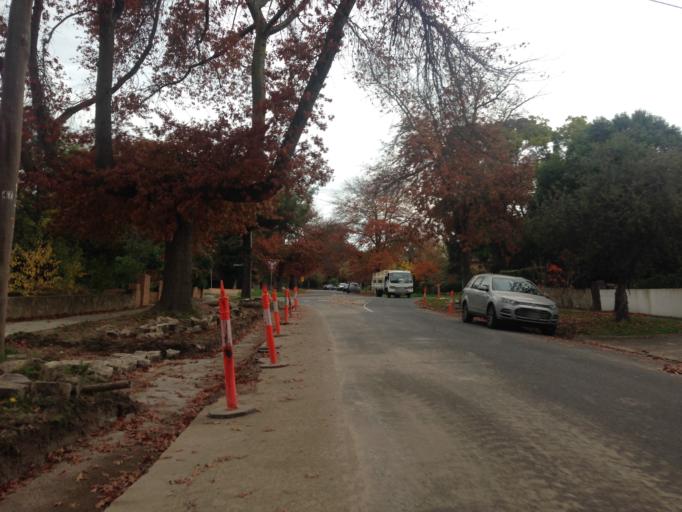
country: AU
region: Victoria
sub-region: Boroondara
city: Kew East
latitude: -37.7892
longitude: 145.0694
